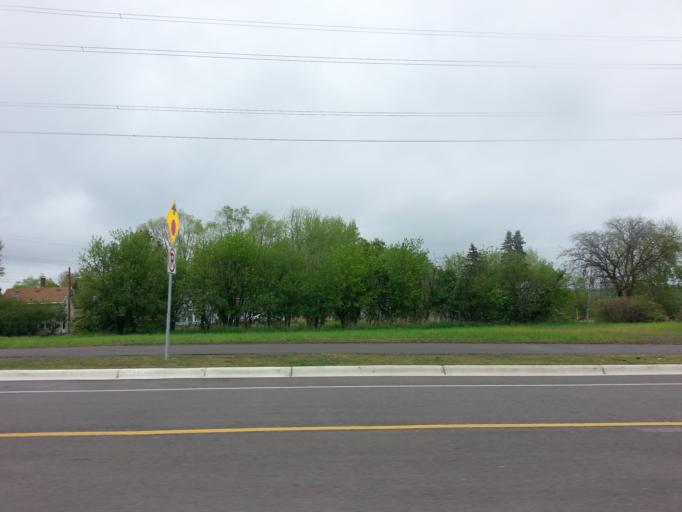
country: US
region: Minnesota
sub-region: Washington County
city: Oak Park Heights
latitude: 45.0299
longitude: -92.7898
